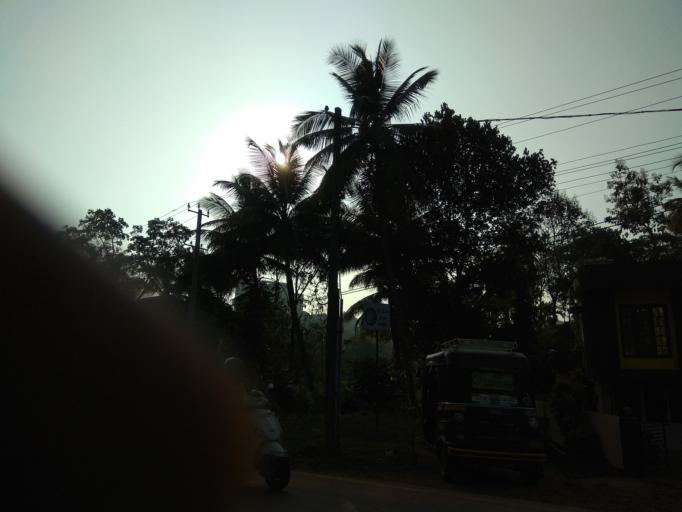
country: IN
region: Karnataka
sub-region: Dakshina Kannada
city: Mangalore
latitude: 12.9120
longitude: 74.8548
